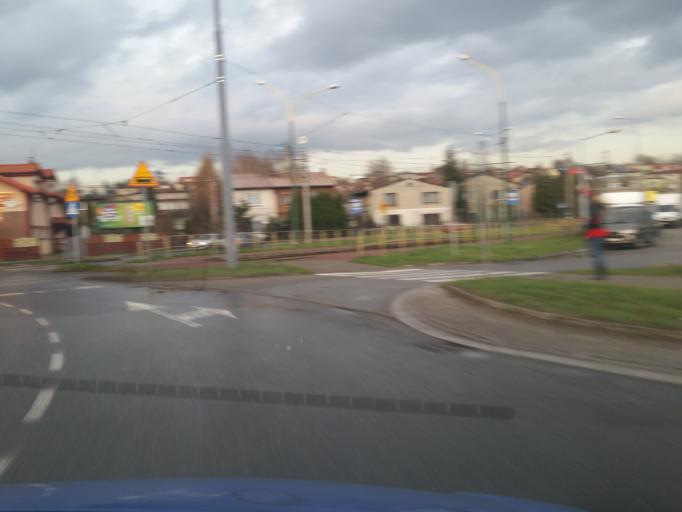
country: PL
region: Silesian Voivodeship
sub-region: Myslowice
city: Myslowice
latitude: 50.2723
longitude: 19.1776
